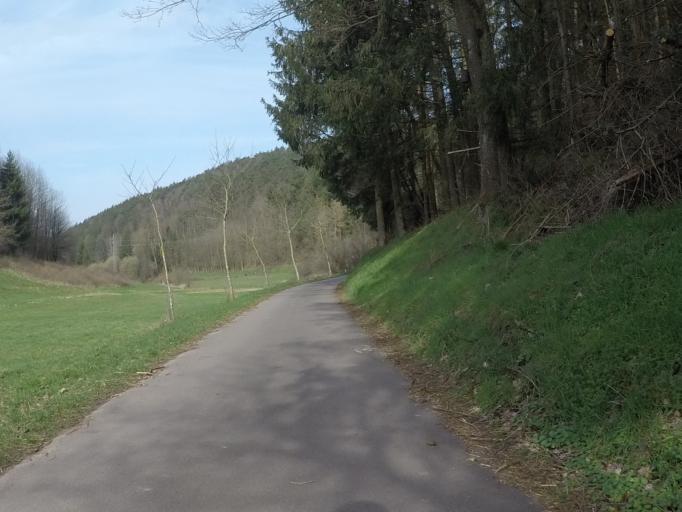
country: DE
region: Rheinland-Pfalz
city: Lug
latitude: 49.1757
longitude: 7.9072
